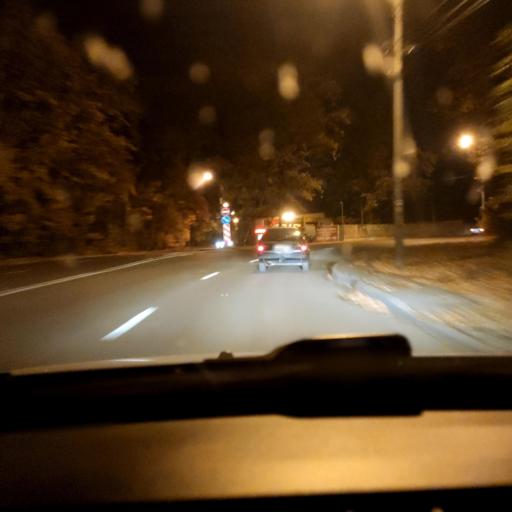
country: RU
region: Voronezj
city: Voronezh
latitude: 51.7257
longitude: 39.2150
